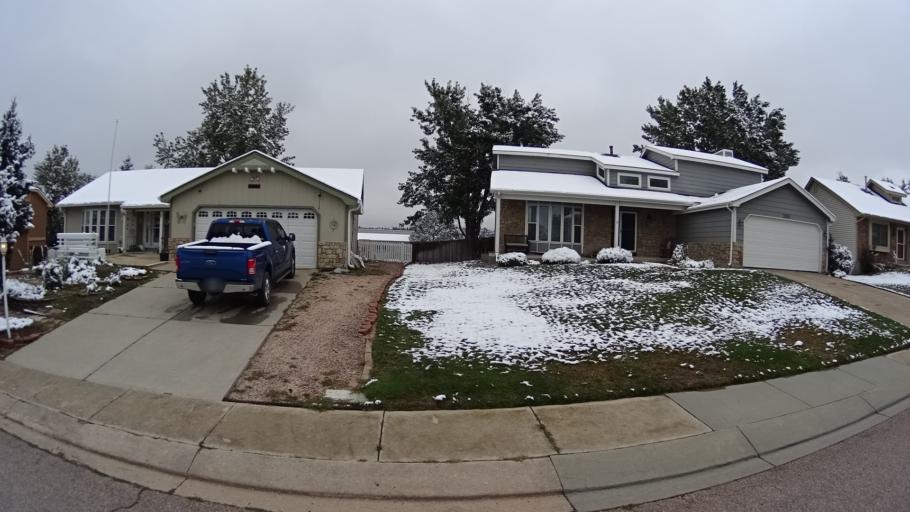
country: US
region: Colorado
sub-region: El Paso County
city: Colorado Springs
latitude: 38.9247
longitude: -104.7782
